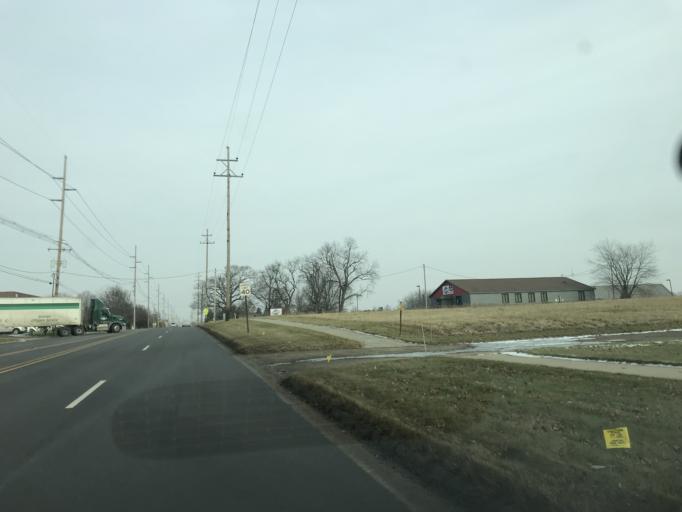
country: US
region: Michigan
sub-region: Ottawa County
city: Holland
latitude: 42.7691
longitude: -86.0773
